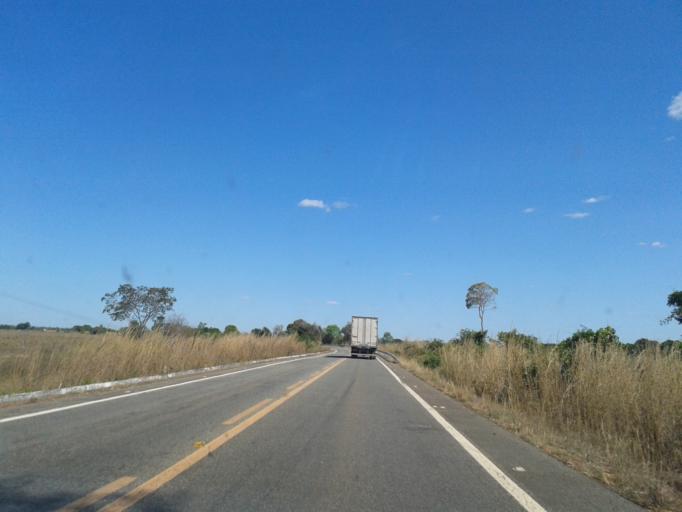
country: BR
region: Goias
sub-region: Sao Miguel Do Araguaia
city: Sao Miguel do Araguaia
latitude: -13.6069
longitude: -50.3207
